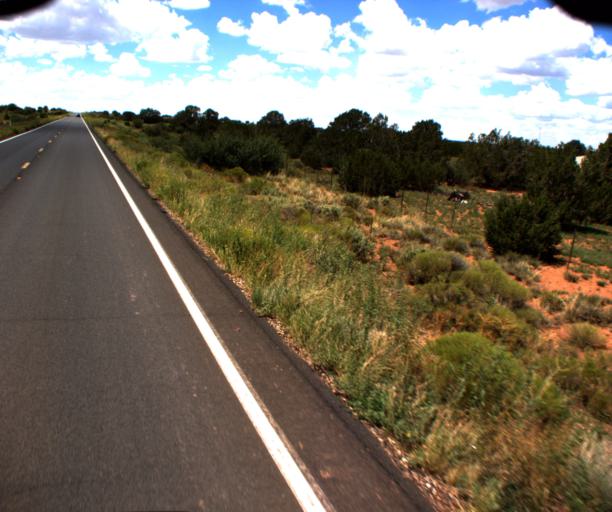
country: US
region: Arizona
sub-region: Coconino County
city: Parks
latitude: 35.6101
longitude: -112.0619
